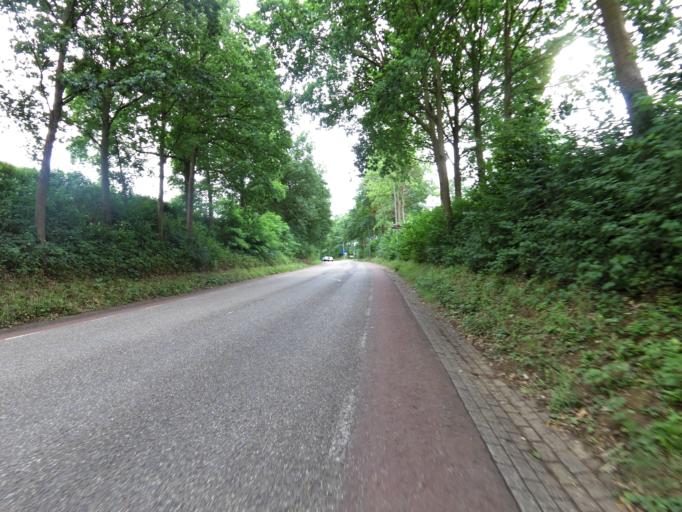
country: NL
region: Limburg
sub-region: Gemeente Voerendaal
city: Klimmen
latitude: 50.8868
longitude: 5.8632
